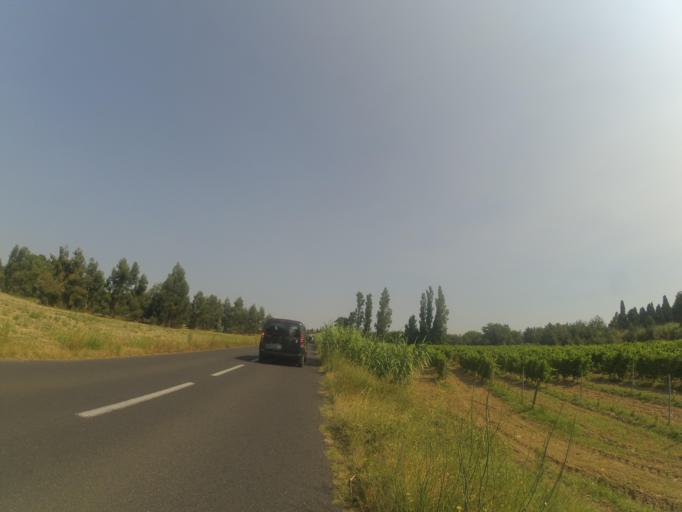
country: FR
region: Languedoc-Roussillon
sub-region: Departement des Pyrenees-Orientales
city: Le Soler
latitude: 42.6911
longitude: 2.7890
